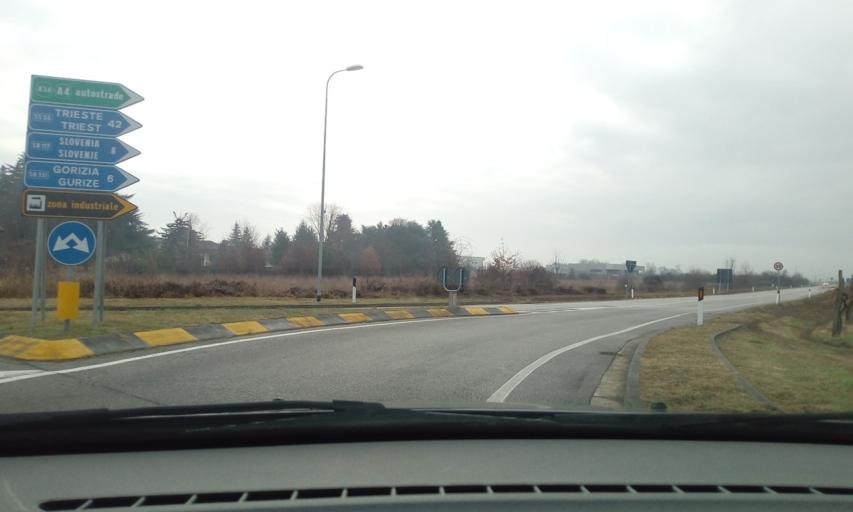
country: IT
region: Friuli Venezia Giulia
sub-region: Provincia di Gorizia
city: Mossa
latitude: 45.9320
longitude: 13.5457
